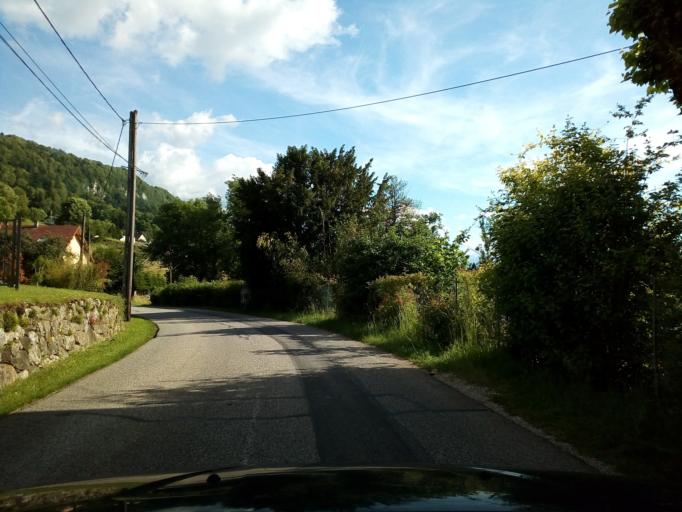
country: FR
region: Rhone-Alpes
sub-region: Departement de la Savoie
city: Saint-Beron
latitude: 45.4849
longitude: 5.7670
